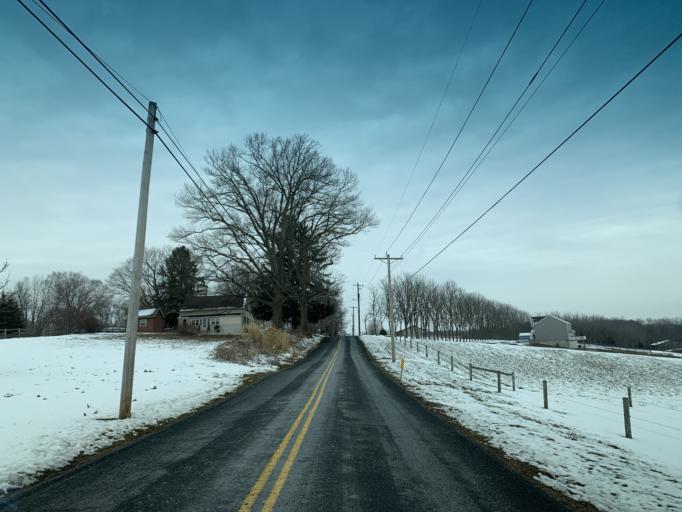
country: US
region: Pennsylvania
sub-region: York County
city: Susquehanna Trails
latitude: 39.7002
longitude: -76.2994
